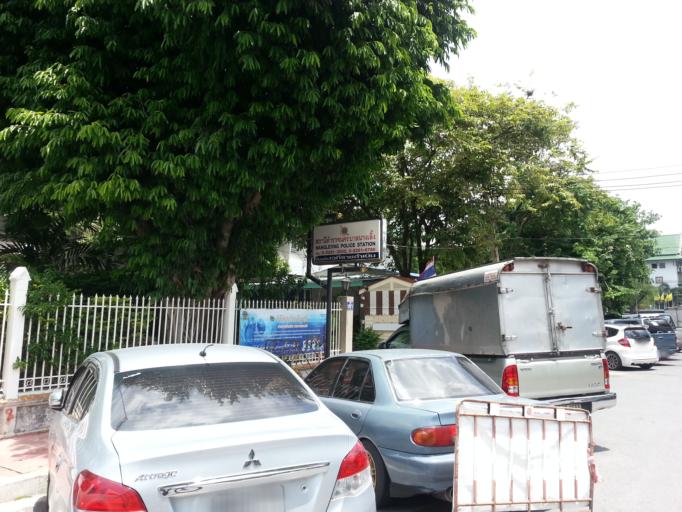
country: TH
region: Bangkok
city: Pom Prap Sattru Phai
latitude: 13.7578
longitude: 100.5075
